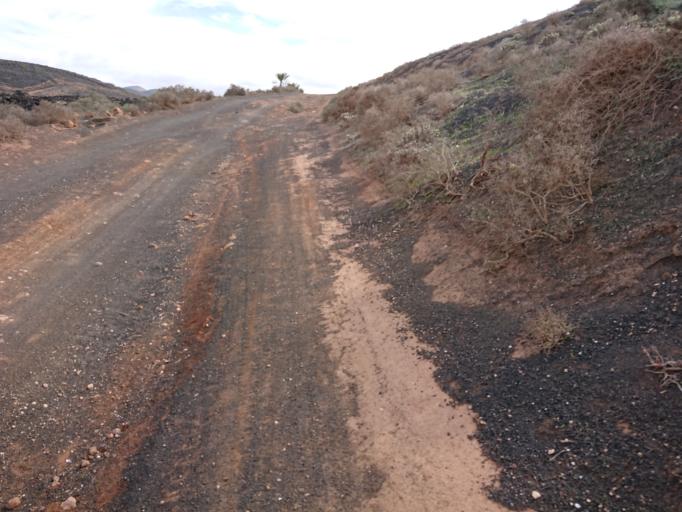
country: ES
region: Canary Islands
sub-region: Provincia de Las Palmas
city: Tinajo
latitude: 29.0195
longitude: -13.6764
